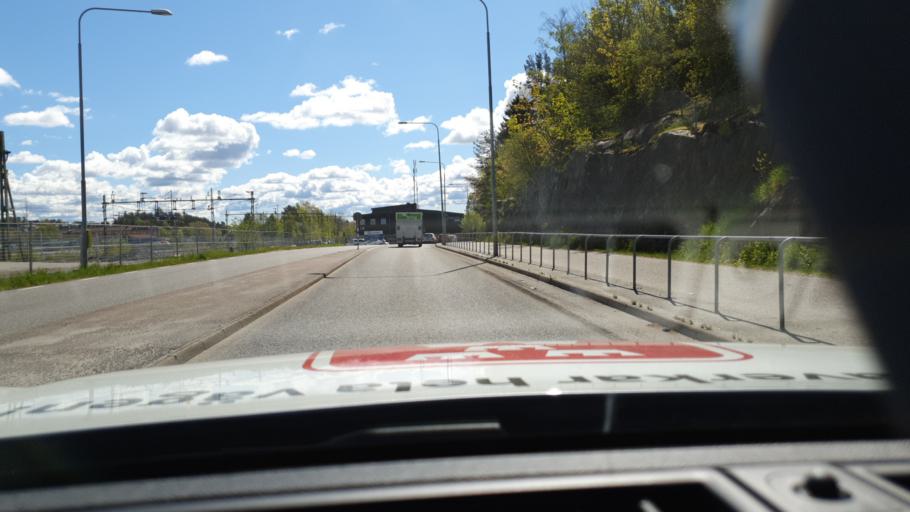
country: SE
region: Stockholm
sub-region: Stockholms Kommun
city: Kista
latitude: 59.3811
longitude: 17.9025
